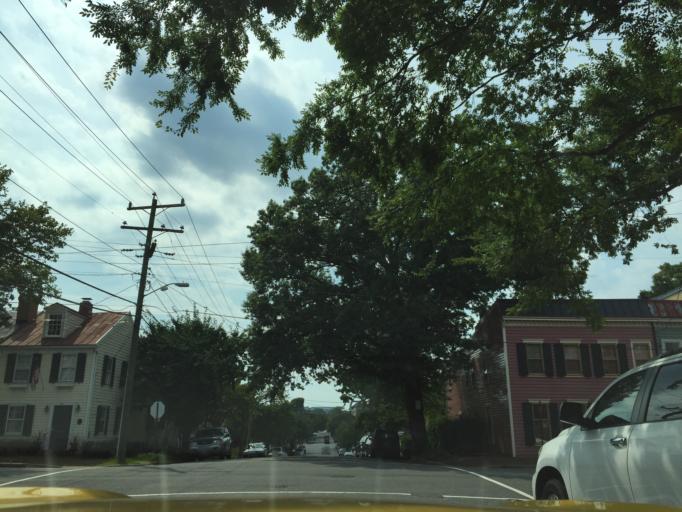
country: US
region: Virginia
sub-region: City of Alexandria
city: Alexandria
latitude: 38.7989
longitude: -77.0435
